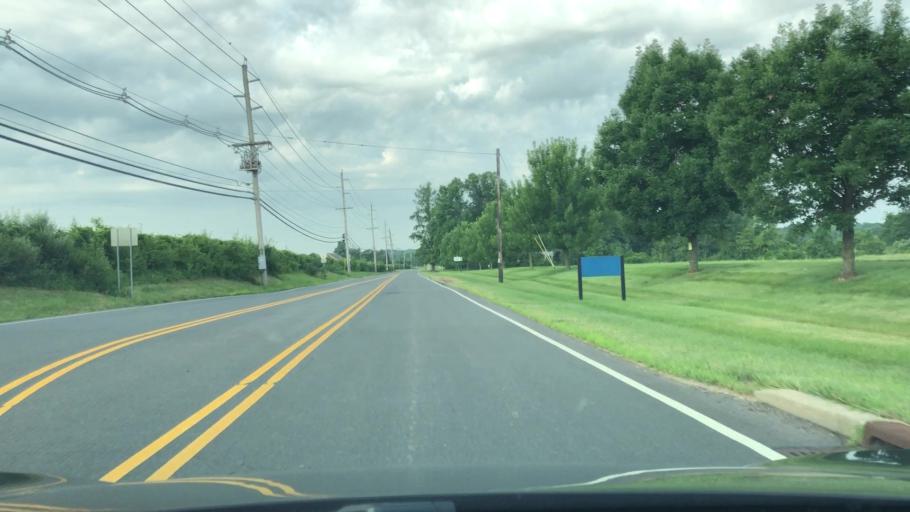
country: US
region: New Jersey
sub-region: Mercer County
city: Pennington
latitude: 40.3389
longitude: -74.7694
